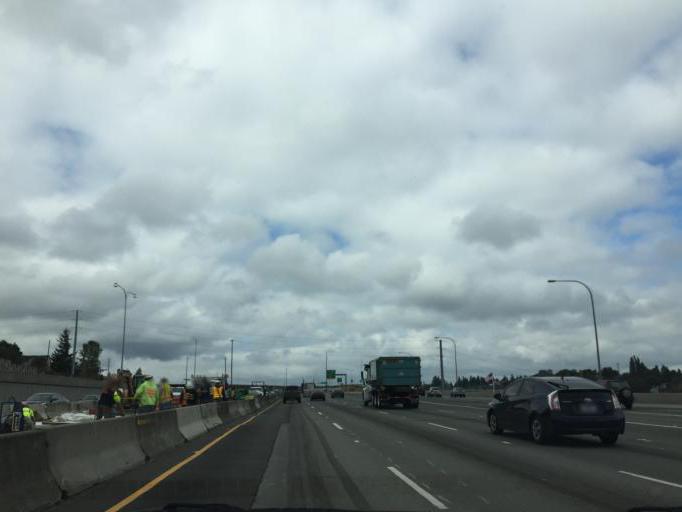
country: US
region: Washington
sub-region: Pierce County
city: Tacoma
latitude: 47.2304
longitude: -122.4511
